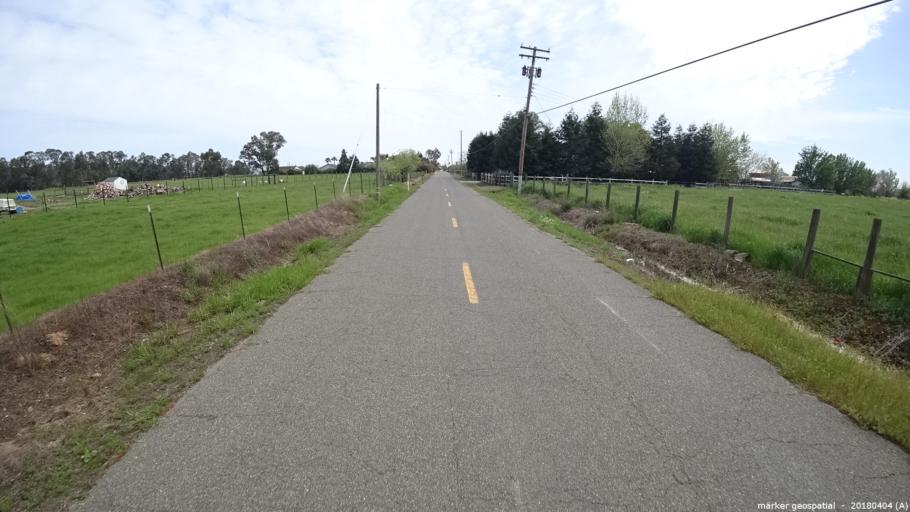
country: US
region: California
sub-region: Sacramento County
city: Herald
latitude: 38.2774
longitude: -121.2352
